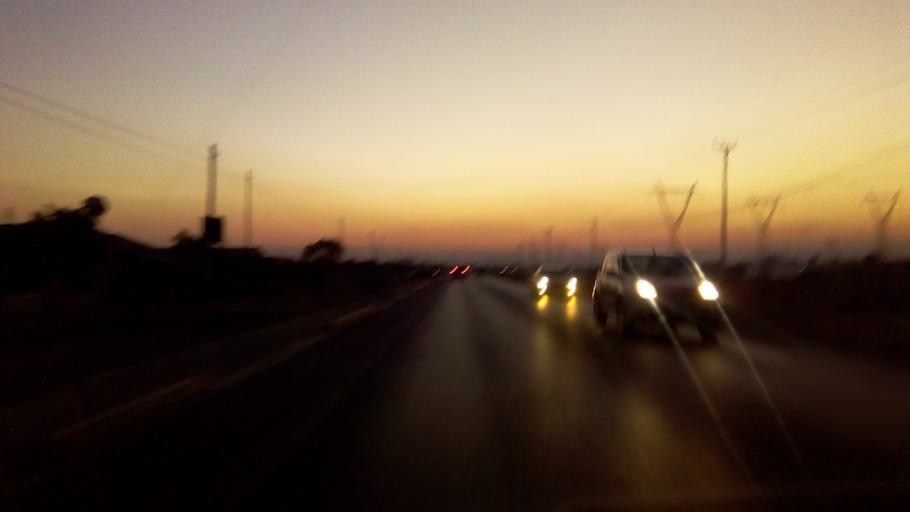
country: ZM
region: Lusaka
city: Lusaka
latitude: -15.4634
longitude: 28.3484
